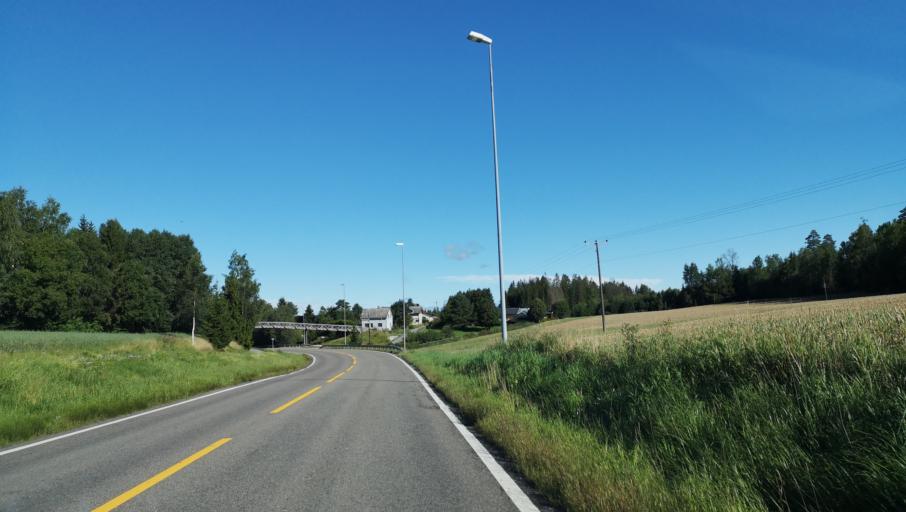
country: NO
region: Ostfold
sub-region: Spydeberg
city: Spydeberg
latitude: 59.5943
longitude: 11.1089
